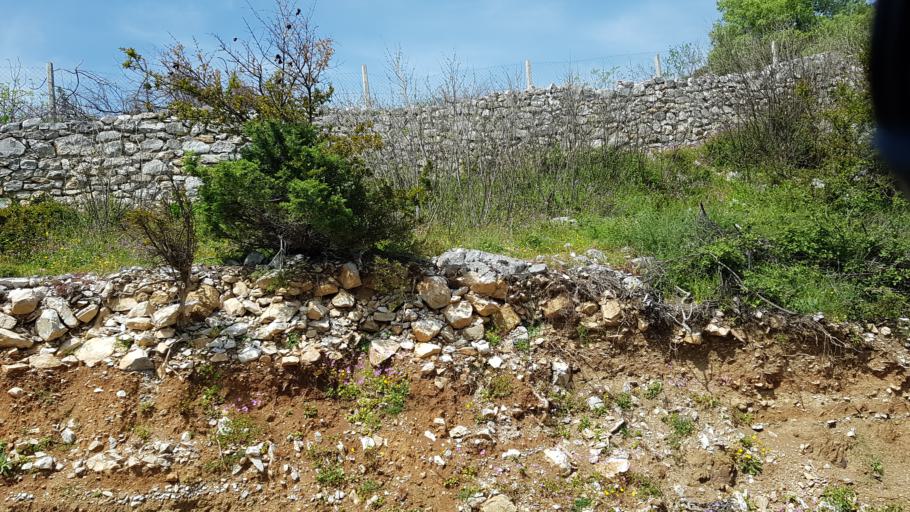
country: AL
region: Shkoder
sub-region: Rrethi i Shkodres
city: Guri i Zi
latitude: 42.1237
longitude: 19.6136
